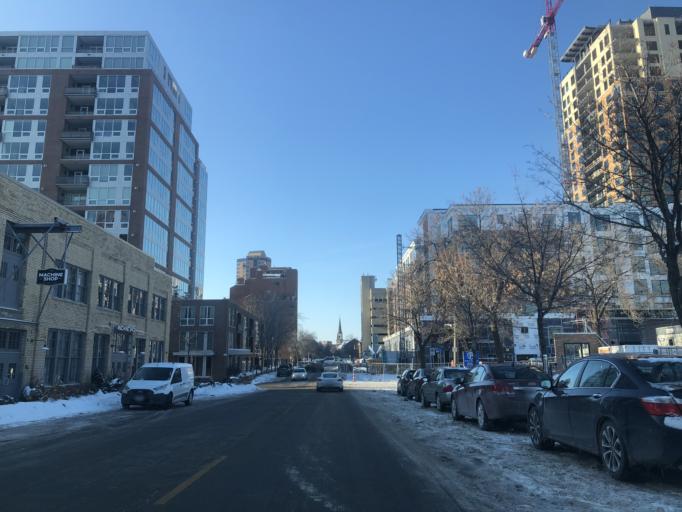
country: US
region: Minnesota
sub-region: Hennepin County
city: Minneapolis
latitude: 44.9844
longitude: -93.2520
